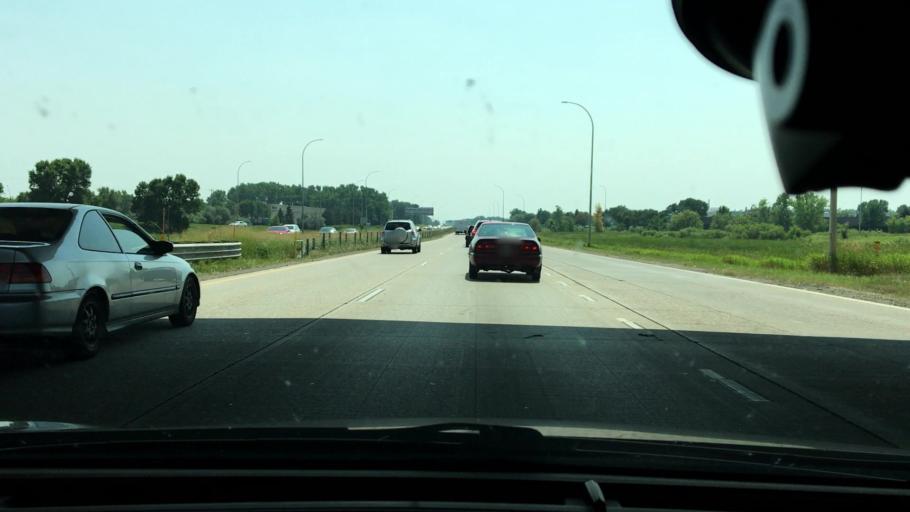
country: US
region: Minnesota
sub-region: Hennepin County
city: Osseo
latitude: 45.0945
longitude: -93.4026
